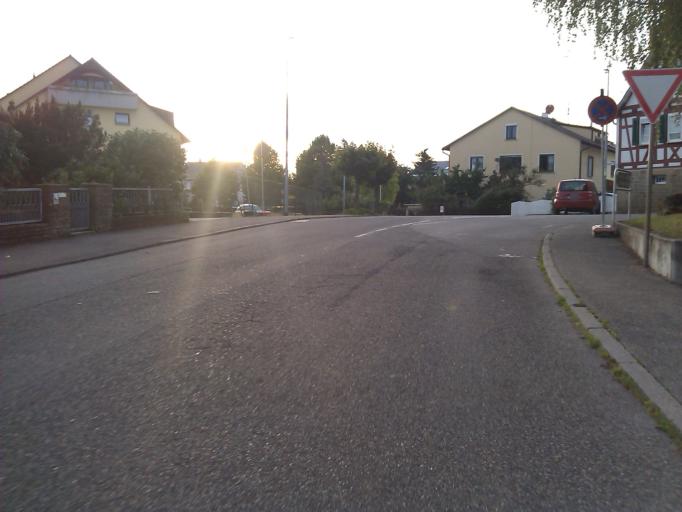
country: DE
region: Baden-Wuerttemberg
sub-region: Regierungsbezirk Stuttgart
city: Brackenheim
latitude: 49.0782
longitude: 9.0702
